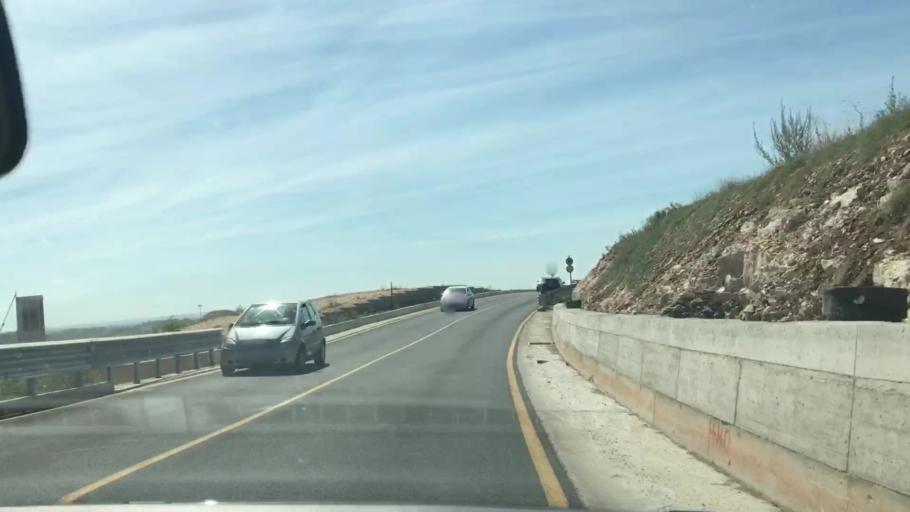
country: IT
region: Apulia
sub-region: Provincia di Bari
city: Altamura
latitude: 40.8096
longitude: 16.5556
